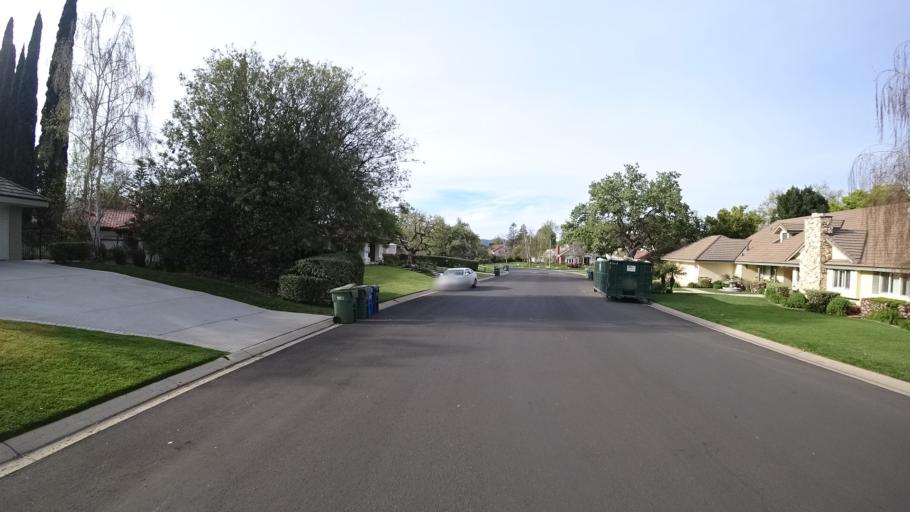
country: US
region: California
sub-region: Ventura County
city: Thousand Oaks
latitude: 34.1952
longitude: -118.8169
